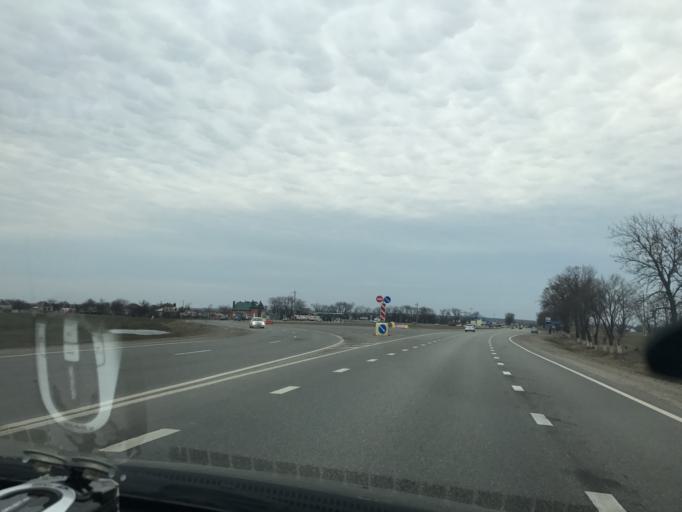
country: RU
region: Krasnodarskiy
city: Novoukrainskoye
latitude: 45.3787
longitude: 40.5569
